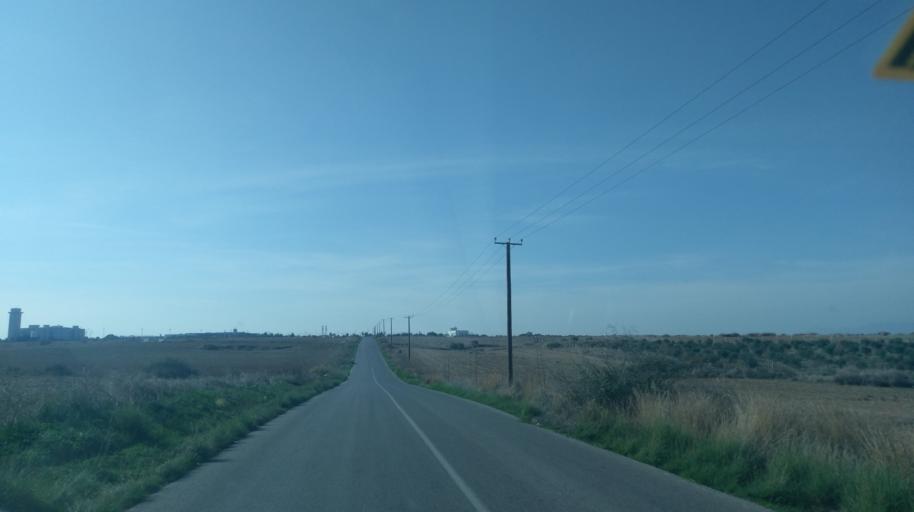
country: CY
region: Larnaka
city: Athienou
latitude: 35.1611
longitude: 33.5163
